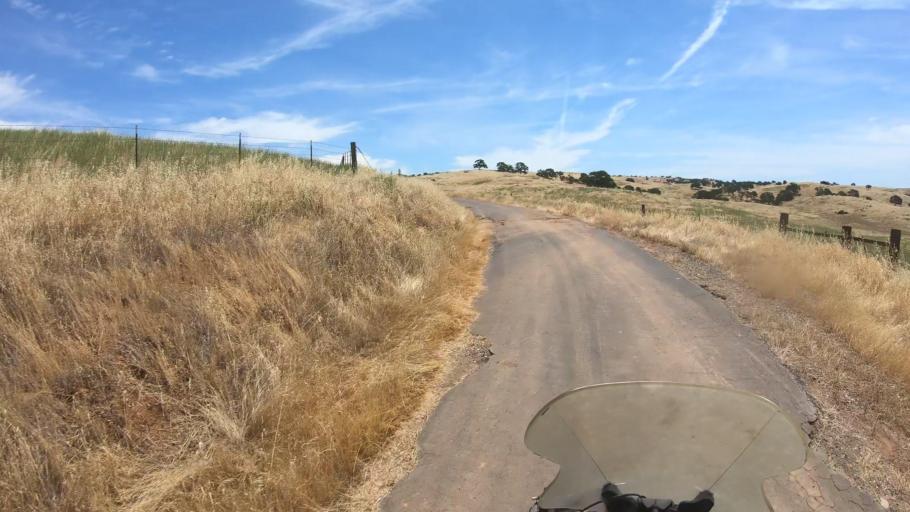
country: US
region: California
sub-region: Tuolumne County
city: Jamestown
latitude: 37.7703
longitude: -120.5523
